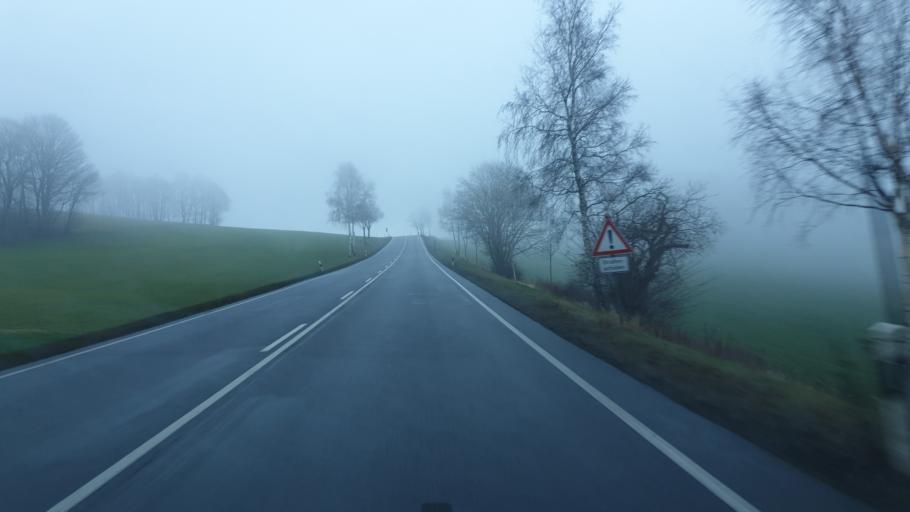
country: DE
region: Saxony
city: Grossolbersdorf
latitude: 50.6969
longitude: 13.1112
